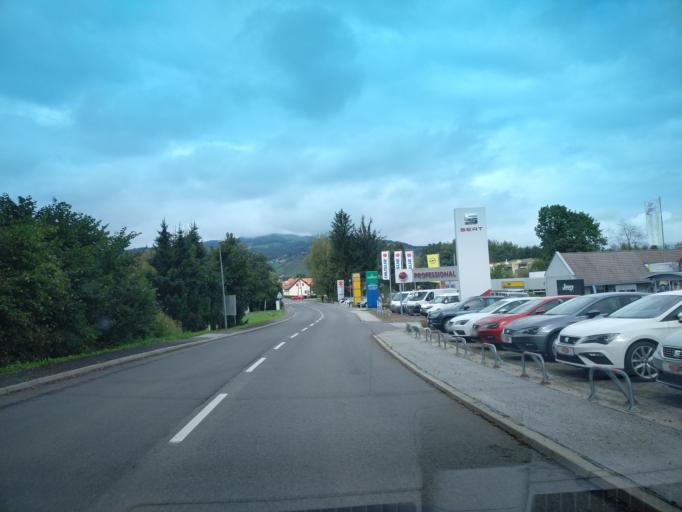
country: AT
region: Styria
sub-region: Politischer Bezirk Deutschlandsberg
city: Deutschlandsberg
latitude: 46.8122
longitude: 15.2260
